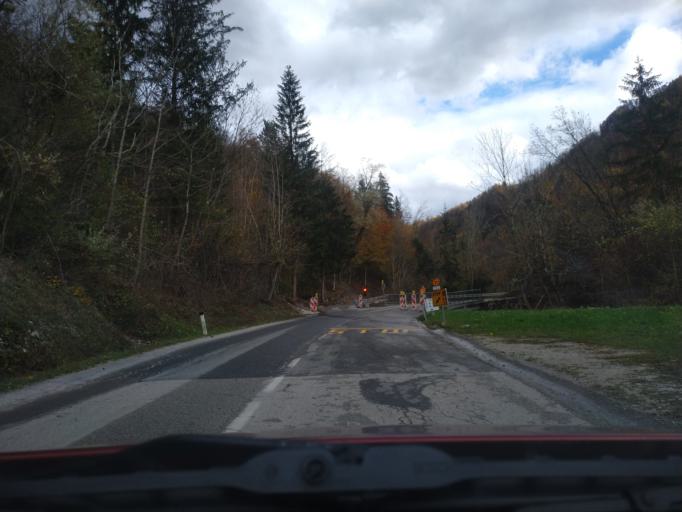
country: SI
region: Kamnik
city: Mekinje
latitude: 46.2629
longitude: 14.6405
